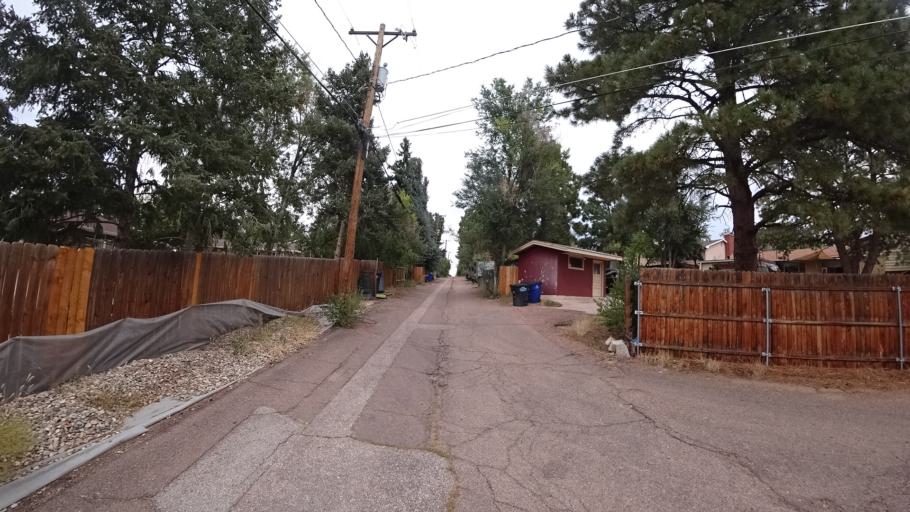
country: US
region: Colorado
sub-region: El Paso County
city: Colorado Springs
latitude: 38.8631
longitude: -104.7855
